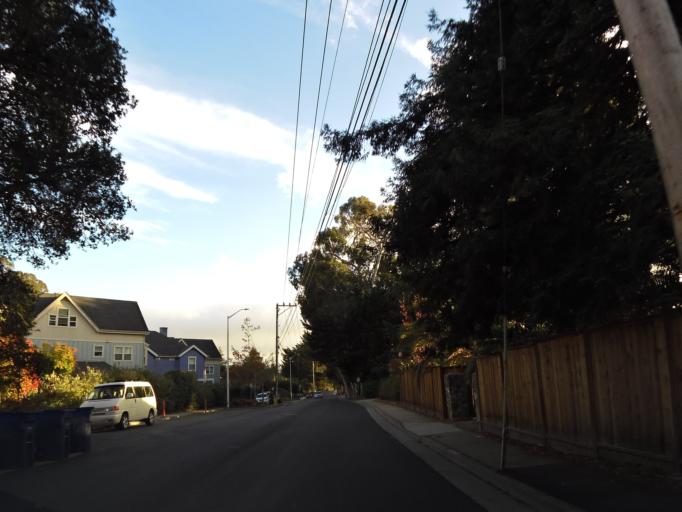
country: US
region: California
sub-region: Santa Cruz County
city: Santa Cruz
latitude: 36.9726
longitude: -122.0585
